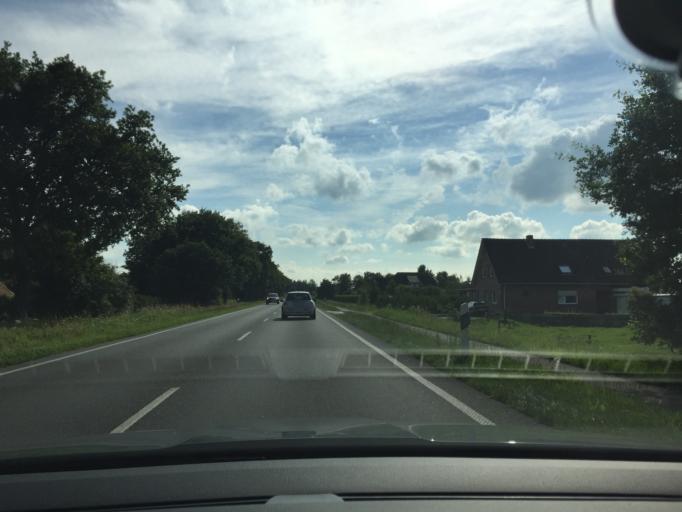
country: DE
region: Lower Saxony
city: Blomberg
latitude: 53.5182
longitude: 7.5651
